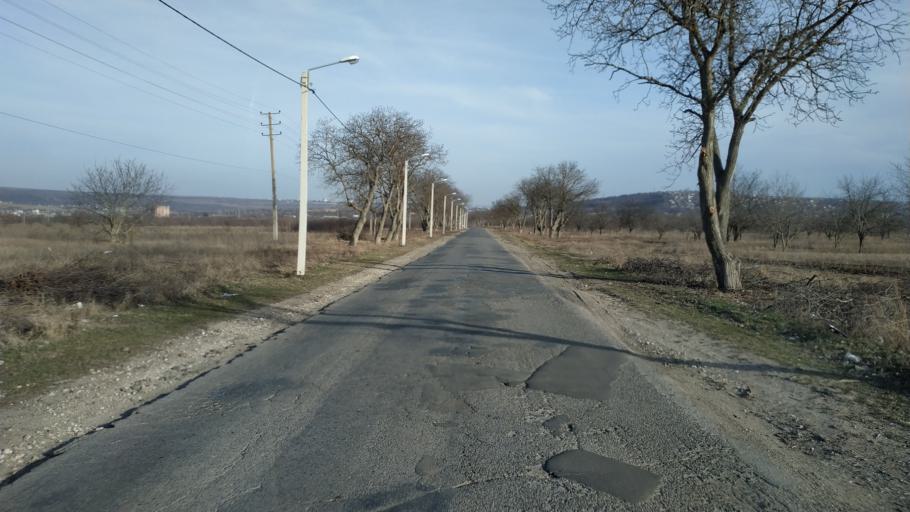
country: MD
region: Chisinau
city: Vatra
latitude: 47.0702
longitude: 28.7165
